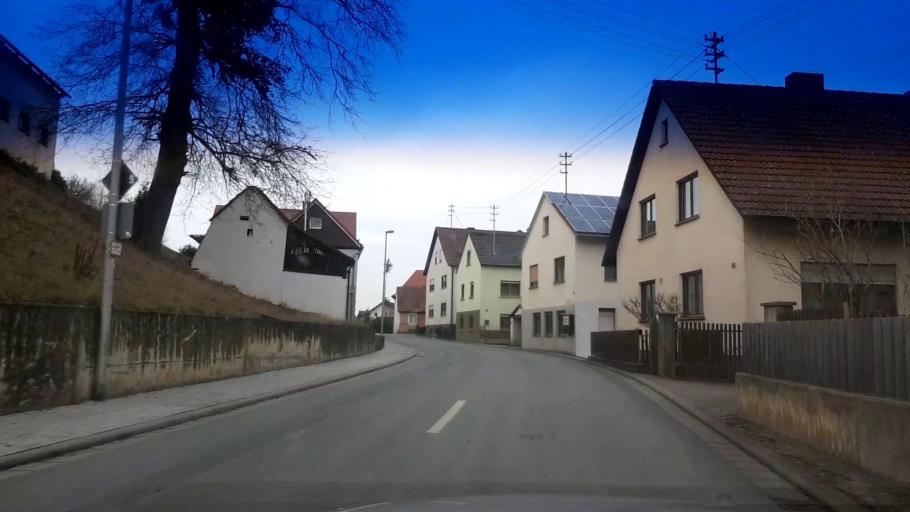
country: DE
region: Bavaria
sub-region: Upper Franconia
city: Altendorf
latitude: 49.7917
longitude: 10.9989
